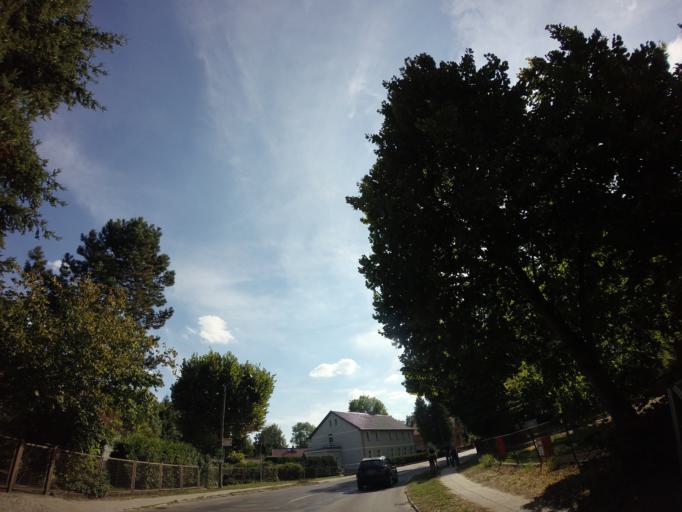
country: DE
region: Brandenburg
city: Rheinsberg
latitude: 53.0965
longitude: 12.8921
